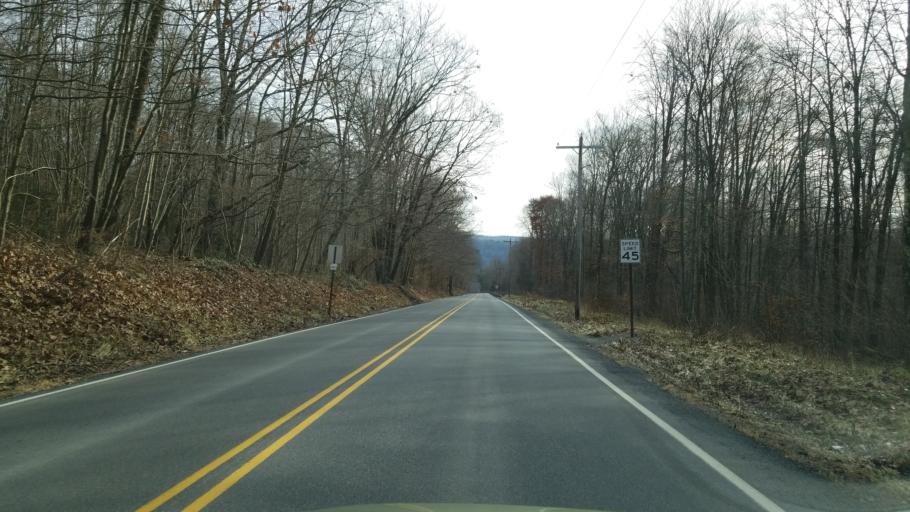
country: US
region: Pennsylvania
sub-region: Indiana County
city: Johnsonburg
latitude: 40.8885
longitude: -78.7760
